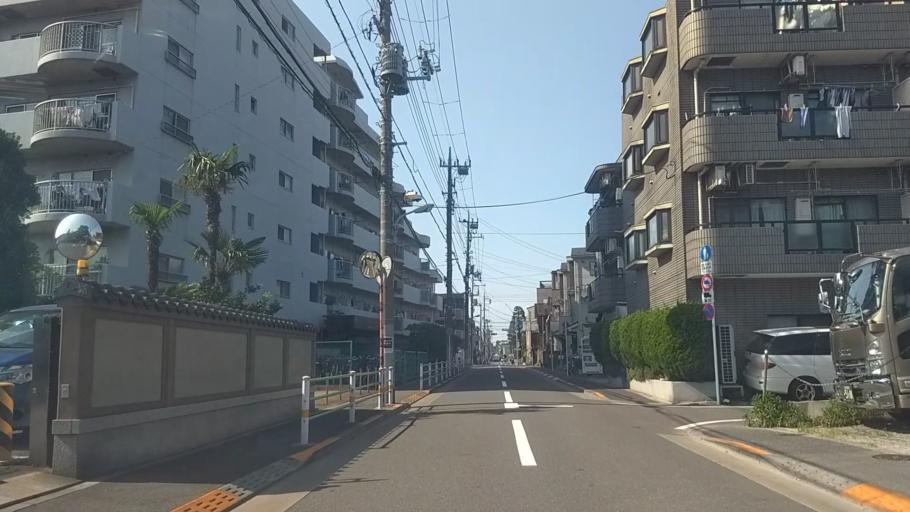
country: JP
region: Kanagawa
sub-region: Kawasaki-shi
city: Kawasaki
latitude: 35.5483
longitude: 139.7362
